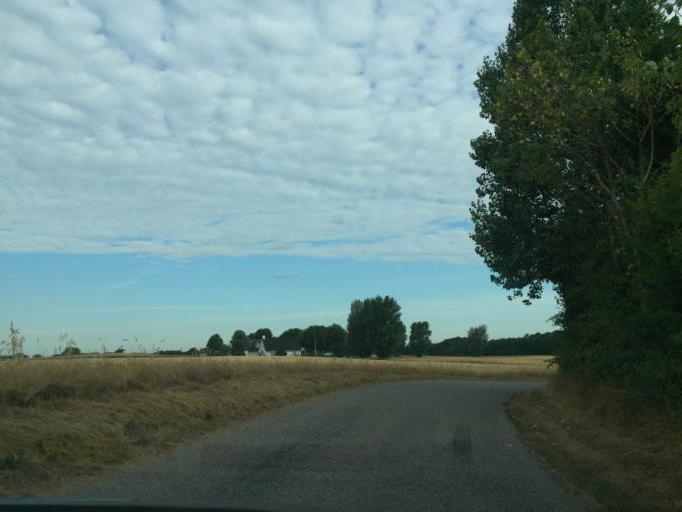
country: DK
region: South Denmark
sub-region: Assens Kommune
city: Assens
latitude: 55.3059
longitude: 9.9729
